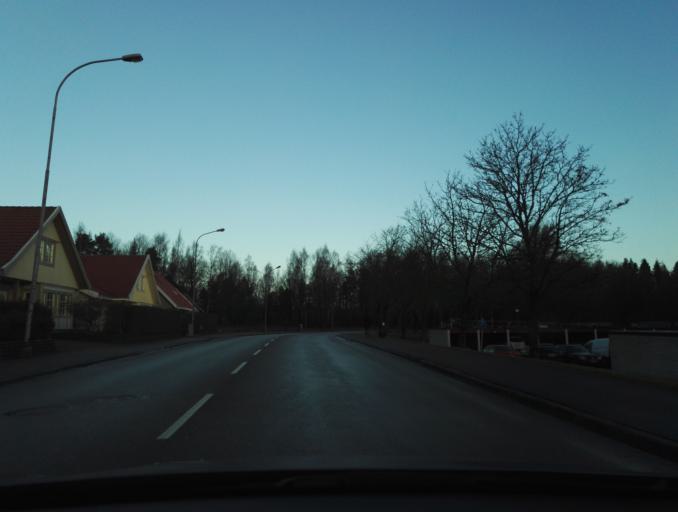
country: SE
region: Kronoberg
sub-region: Vaxjo Kommun
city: Vaexjoe
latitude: 56.8972
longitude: 14.7864
